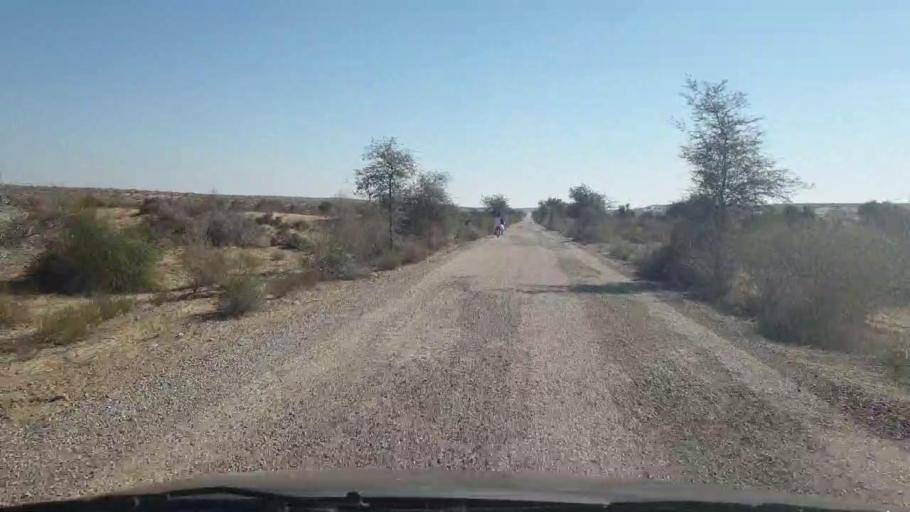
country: PK
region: Sindh
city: Bozdar
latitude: 27.0335
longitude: 68.7000
